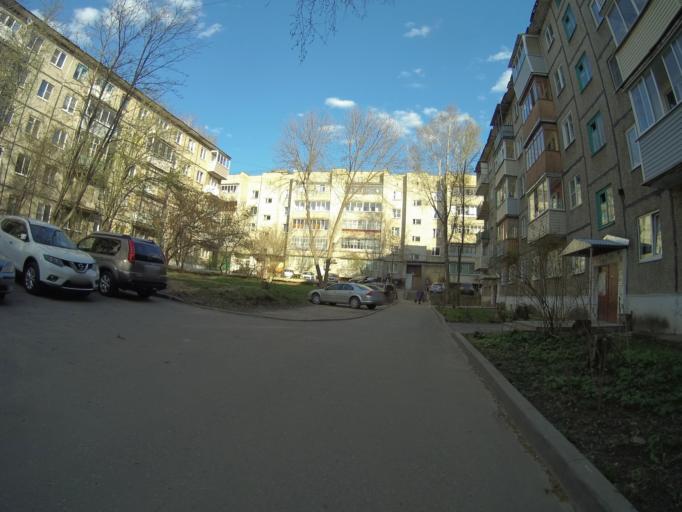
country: RU
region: Vladimir
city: Vladimir
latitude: 56.1337
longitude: 40.3571
